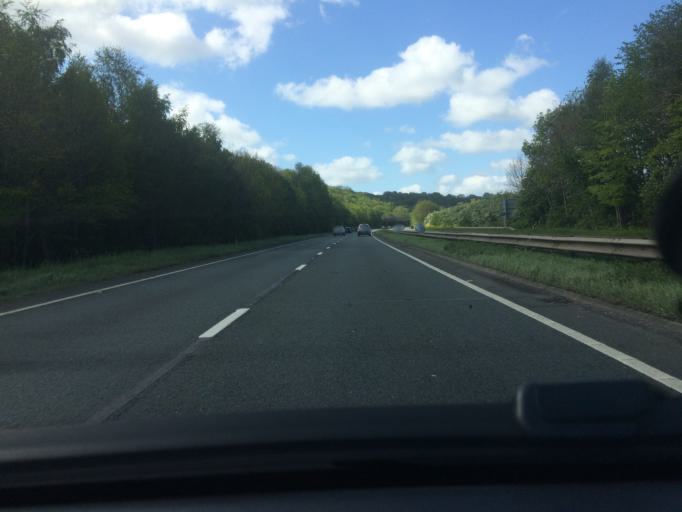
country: GB
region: Wales
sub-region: Wrexham
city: Gresford
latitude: 53.0977
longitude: -2.9650
